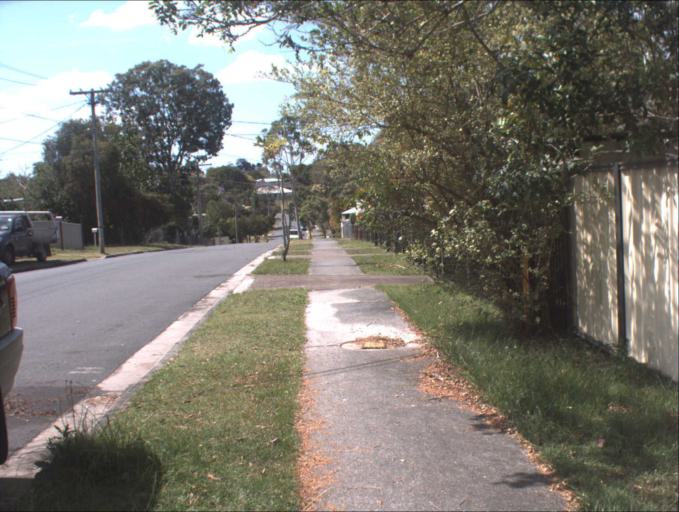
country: AU
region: Queensland
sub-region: Logan
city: Woodridge
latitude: -27.6320
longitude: 153.1009
